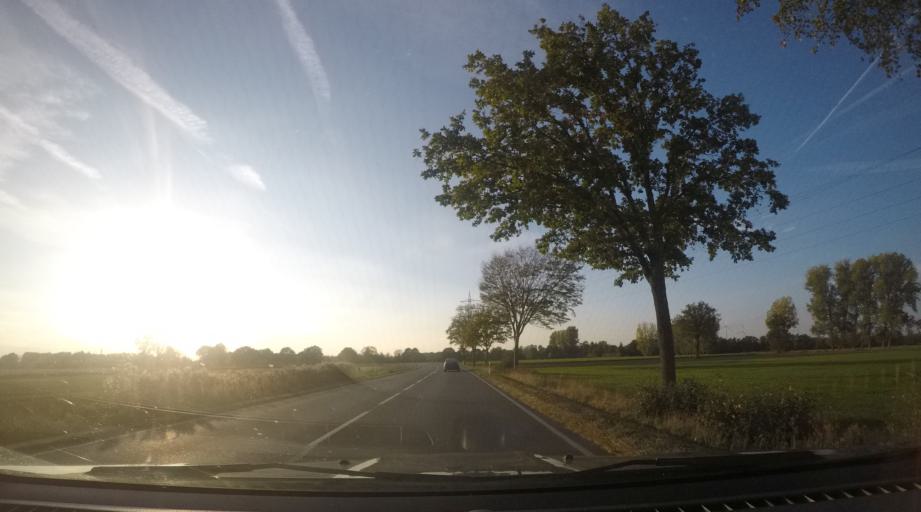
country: DE
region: North Rhine-Westphalia
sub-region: Regierungsbezirk Dusseldorf
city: Hamminkeln
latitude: 51.7728
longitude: 6.6004
